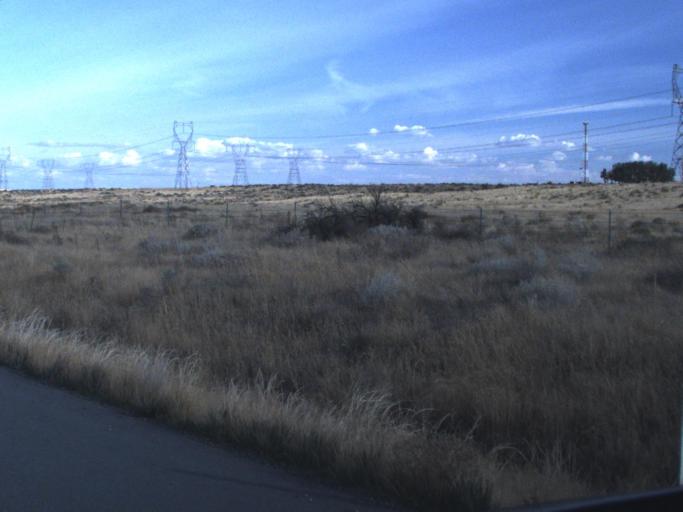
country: US
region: Oregon
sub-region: Morrow County
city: Irrigon
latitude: 45.9453
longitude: -119.4936
